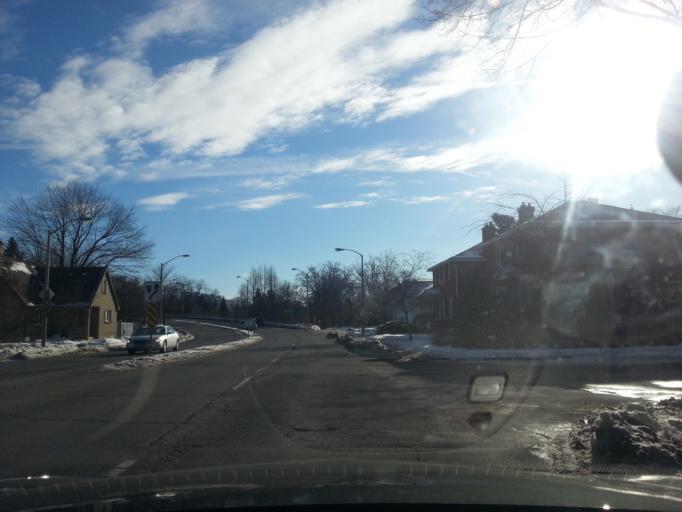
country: CA
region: Ontario
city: Ottawa
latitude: 45.4011
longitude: -75.6735
